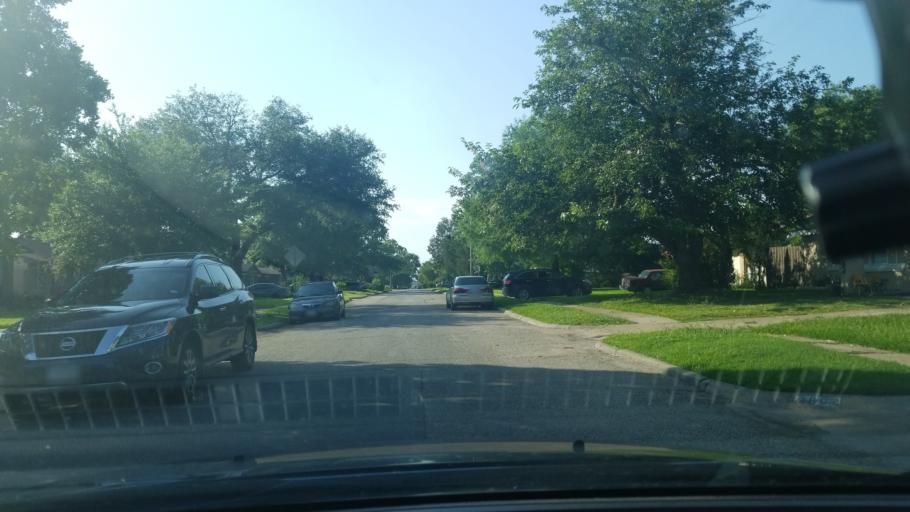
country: US
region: Texas
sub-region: Dallas County
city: Mesquite
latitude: 32.8150
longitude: -96.6397
